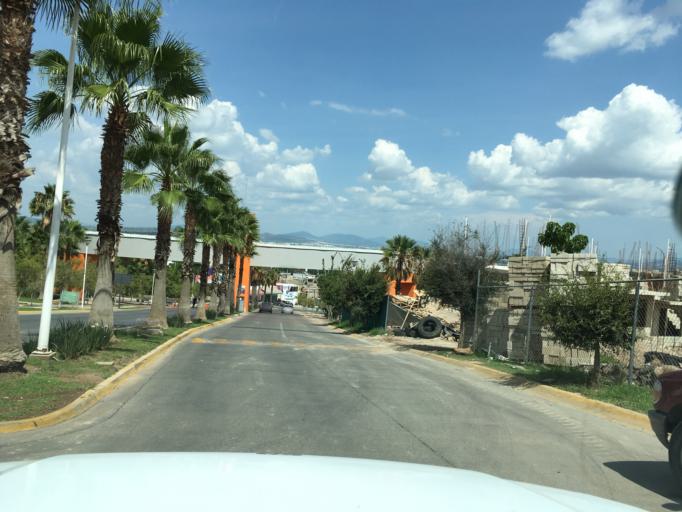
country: MX
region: Jalisco
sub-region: Tlajomulco de Zuniga
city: Altus Bosques
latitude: 20.5880
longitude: -103.3601
